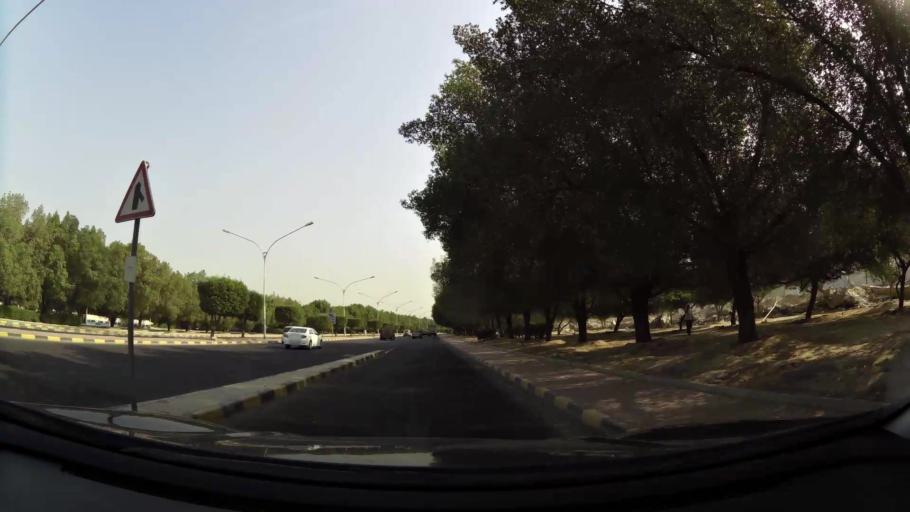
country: KW
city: Bayan
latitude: 29.2862
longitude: 48.0589
